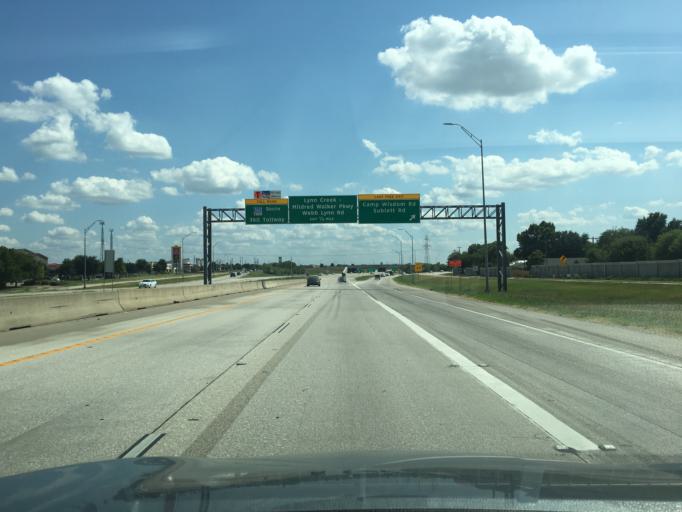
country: US
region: Texas
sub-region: Tarrant County
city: Arlington
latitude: 32.6547
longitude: -97.0621
